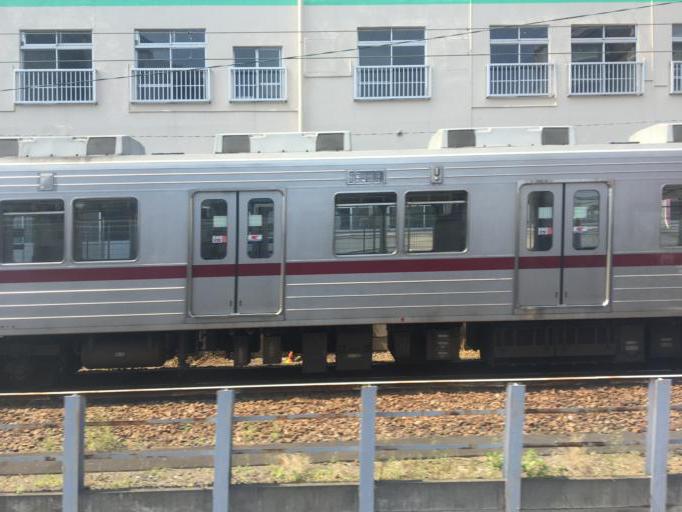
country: JP
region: Saitama
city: Wako
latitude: 35.7795
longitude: 139.6300
